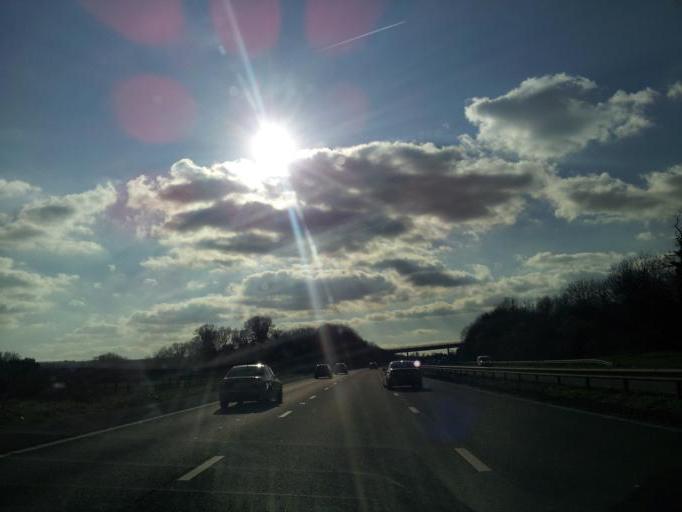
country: GB
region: England
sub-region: Somerset
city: Taunton
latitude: 50.9798
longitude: -3.1221
